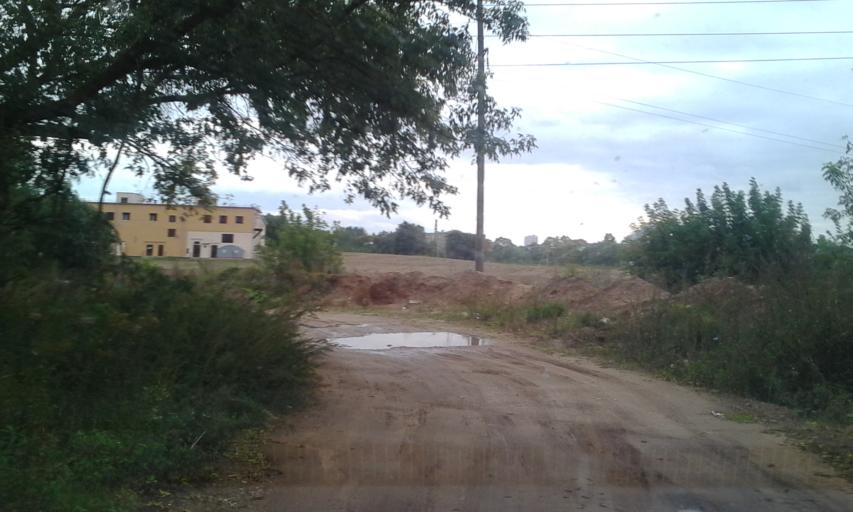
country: BY
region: Minsk
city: Minsk
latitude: 53.9484
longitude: 27.5689
